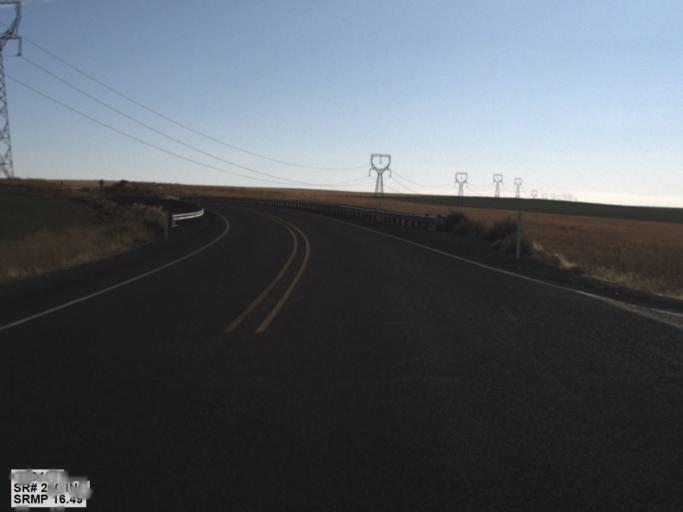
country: US
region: Washington
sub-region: Franklin County
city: Connell
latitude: 46.6203
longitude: -118.7110
